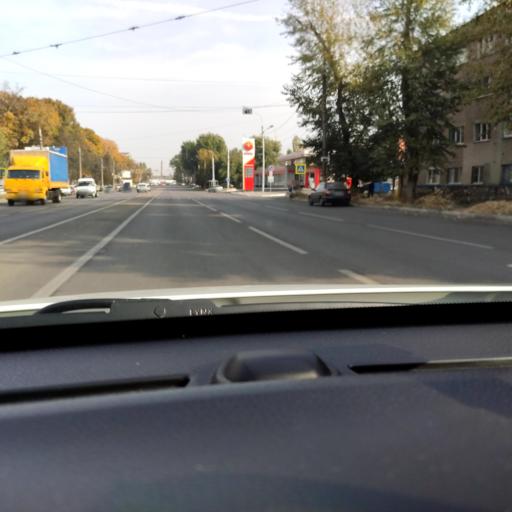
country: RU
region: Voronezj
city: Voronezh
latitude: 51.6758
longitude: 39.1696
